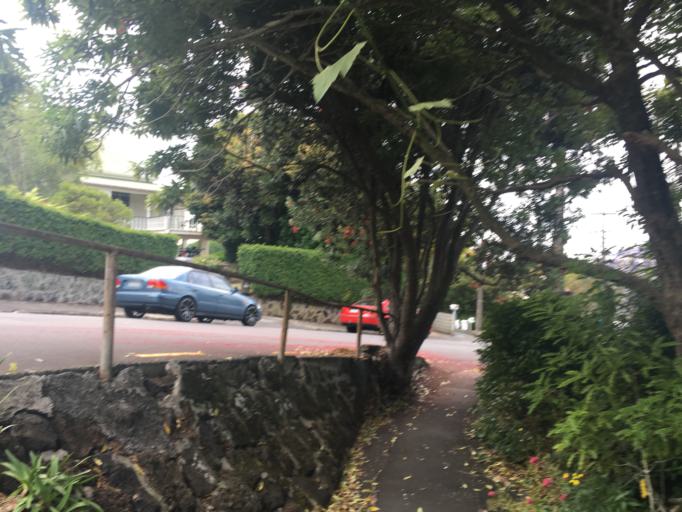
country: NZ
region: Auckland
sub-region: Auckland
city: Auckland
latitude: -36.8297
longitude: 174.8005
